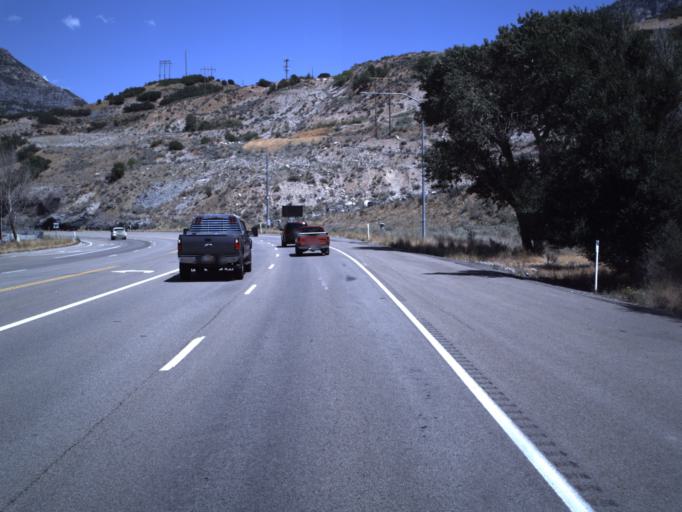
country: US
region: Utah
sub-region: Utah County
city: Orem
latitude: 40.3231
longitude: -111.6447
